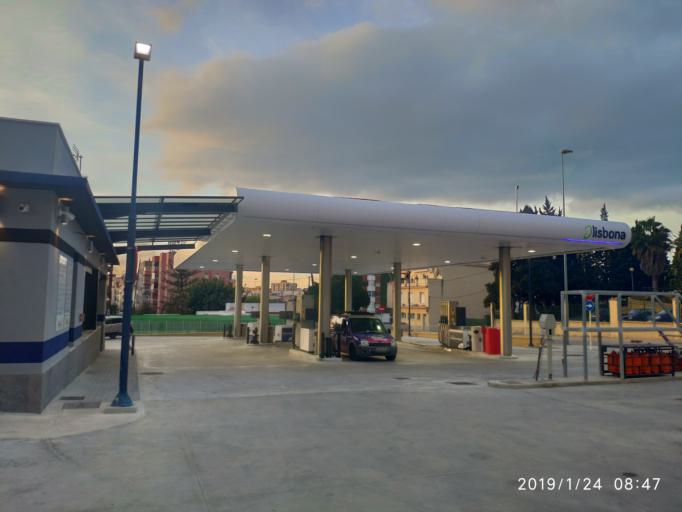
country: ES
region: Andalusia
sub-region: Provincia de Malaga
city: Velez-Malaga
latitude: 36.7459
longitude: -4.0963
